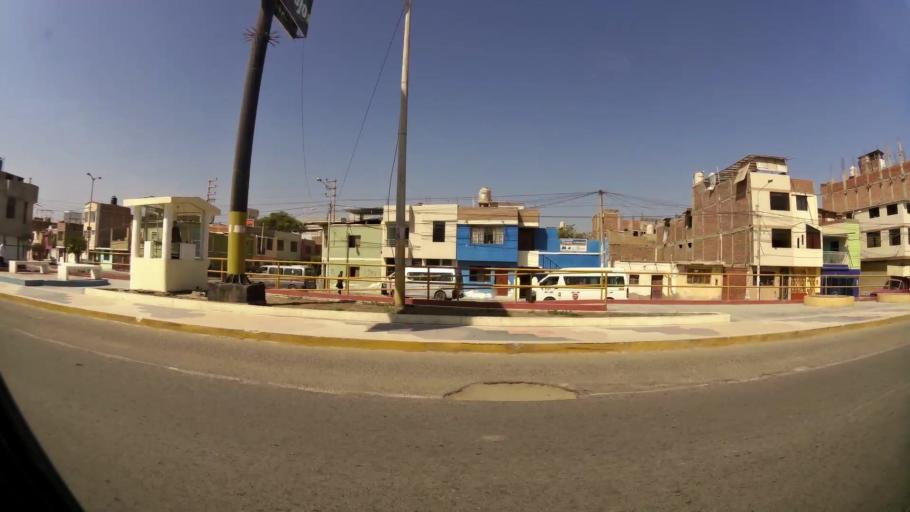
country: PE
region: Lambayeque
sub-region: Provincia de Chiclayo
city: Chiclayo
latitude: -6.7805
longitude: -79.8344
